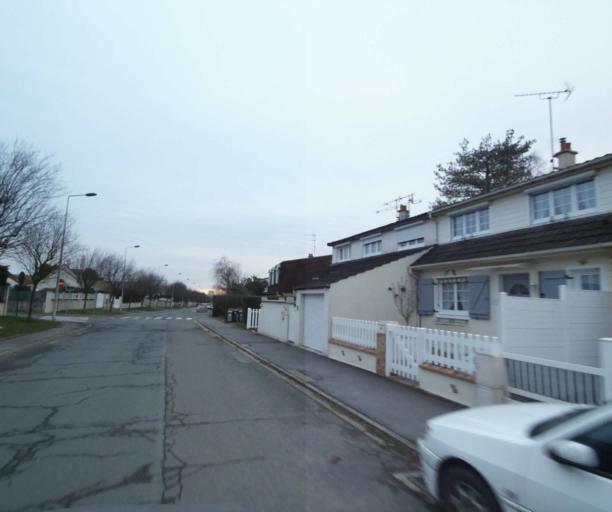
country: FR
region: Ile-de-France
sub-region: Departement de Seine-et-Marne
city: Dammartin-en-Goele
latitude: 49.0613
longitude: 2.6861
